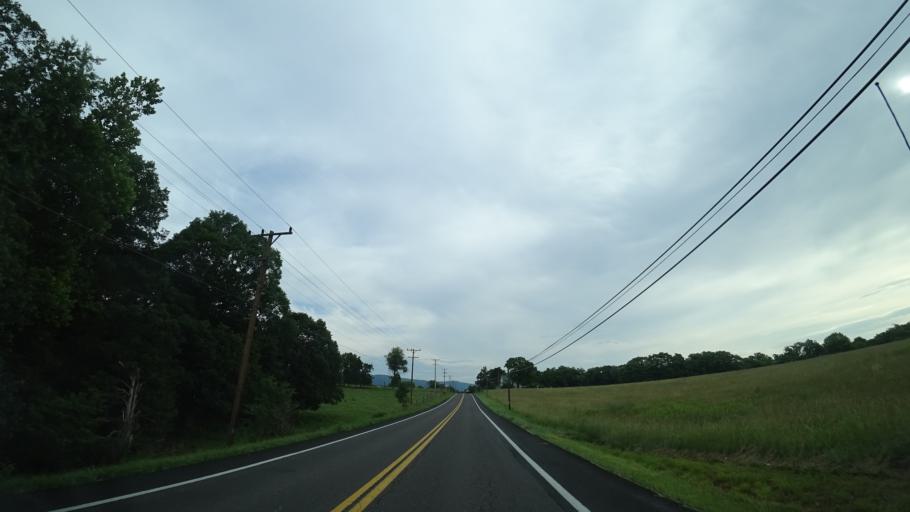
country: US
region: Virginia
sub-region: Page County
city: Luray
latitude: 38.7543
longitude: -78.4011
